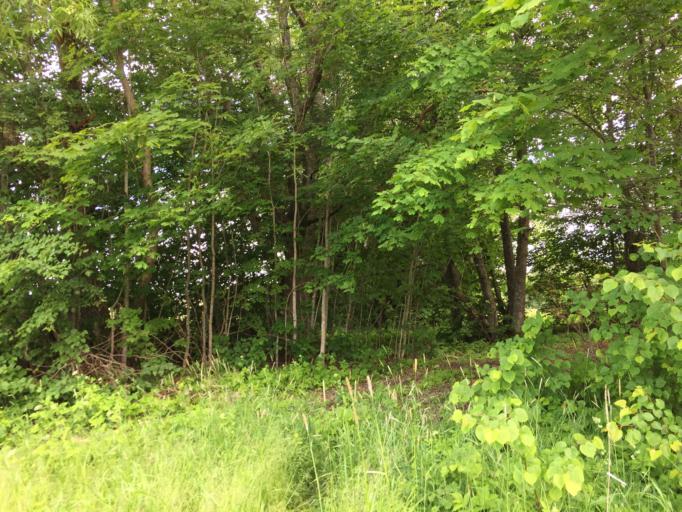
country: LV
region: Apes Novads
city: Ape
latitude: 57.5432
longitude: 26.4541
